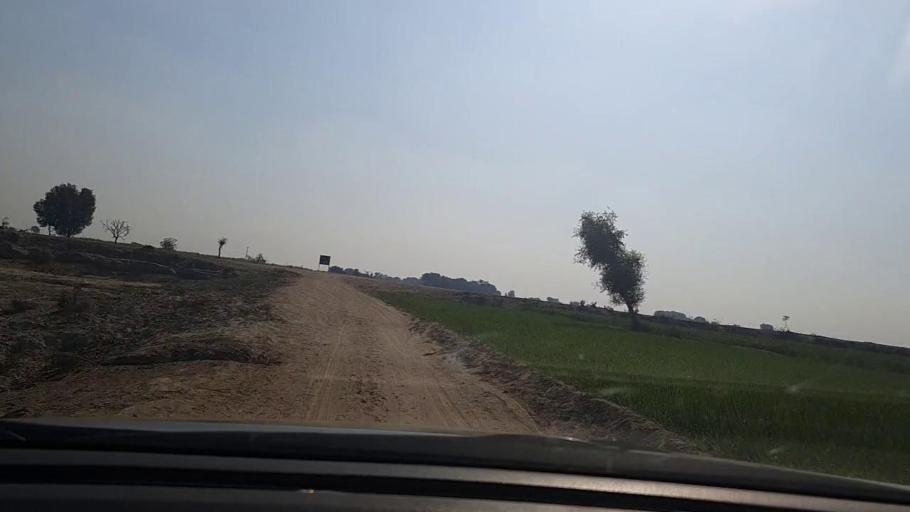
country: PK
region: Sindh
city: Sann
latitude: 26.2633
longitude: 68.0741
